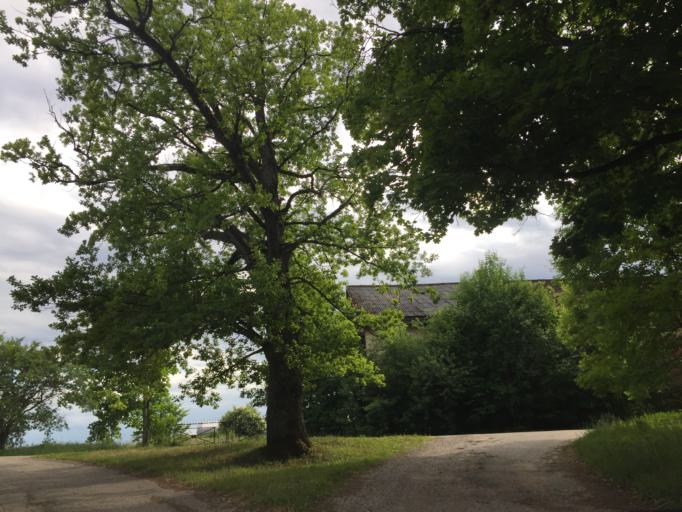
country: LV
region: Pargaujas
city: Stalbe
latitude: 57.3462
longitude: 24.9476
